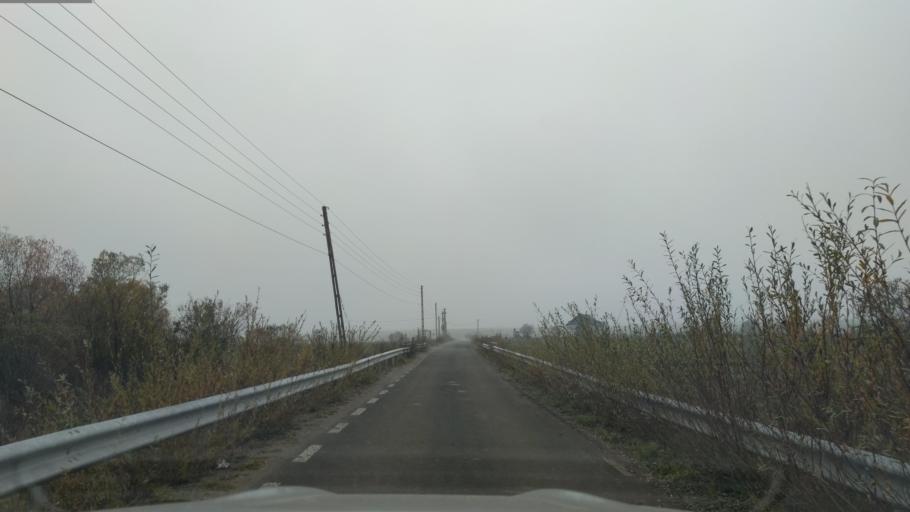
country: RO
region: Harghita
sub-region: Comuna Remetea
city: Remetea
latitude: 46.8125
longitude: 25.4226
